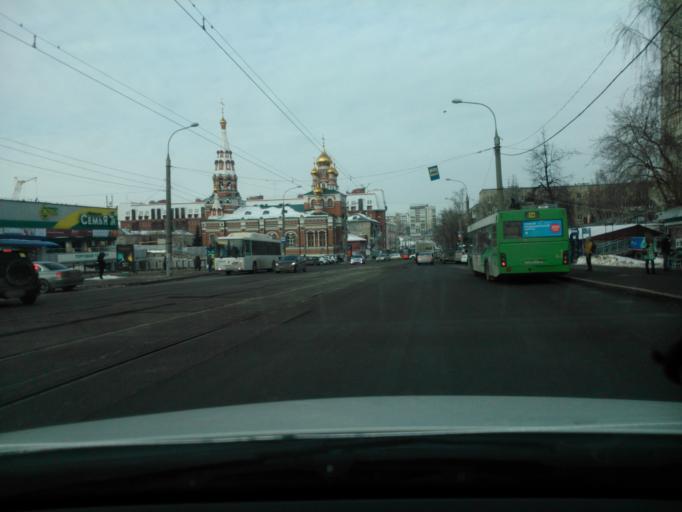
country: RU
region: Perm
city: Perm
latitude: 58.0044
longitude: 56.2224
